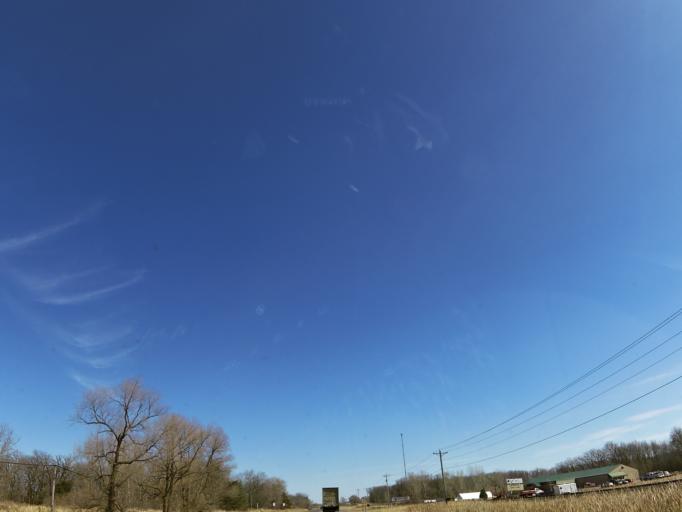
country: US
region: Minnesota
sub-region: Hennepin County
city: Medina
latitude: 45.0563
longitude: -93.5824
